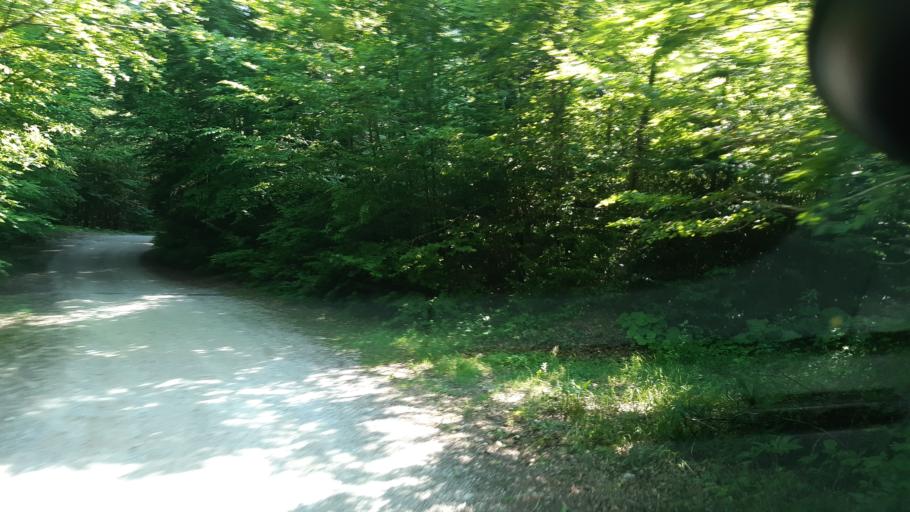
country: SI
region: Trzic
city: Bistrica pri Trzicu
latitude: 46.3744
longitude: 14.2738
